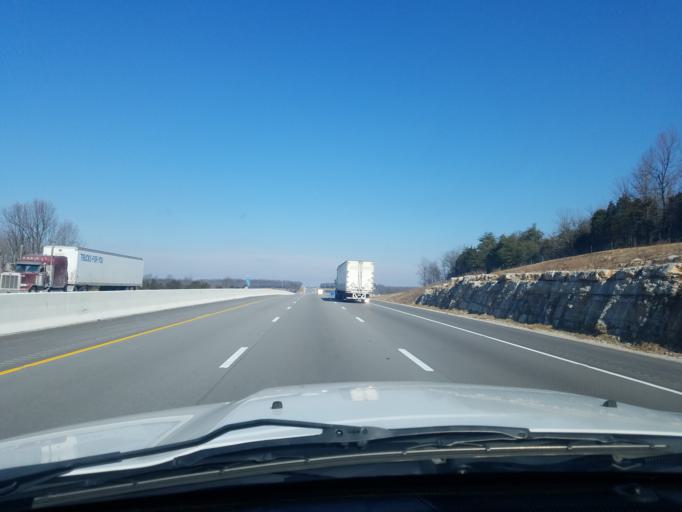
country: US
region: Kentucky
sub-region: Hart County
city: Munfordville
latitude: 37.4474
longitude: -85.8833
